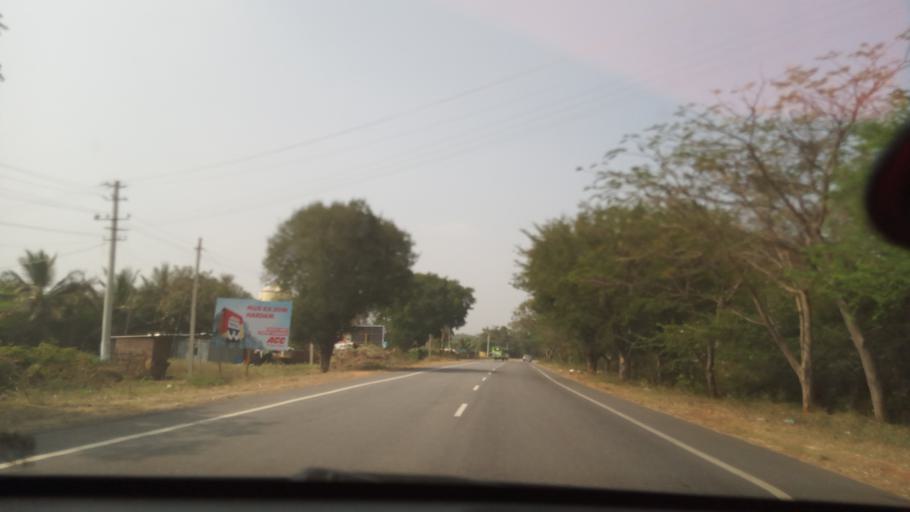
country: IN
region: Karnataka
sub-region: Mysore
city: Nanjangud
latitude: 12.0771
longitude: 76.7384
